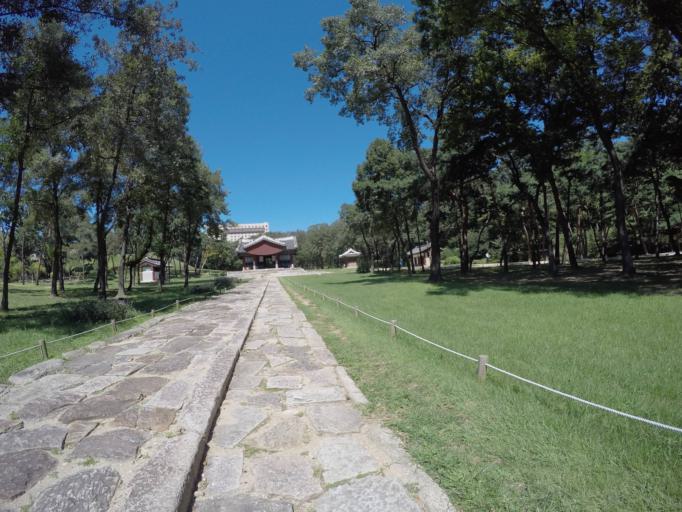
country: KR
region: Seoul
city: Seoul
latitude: 37.5076
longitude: 127.0466
